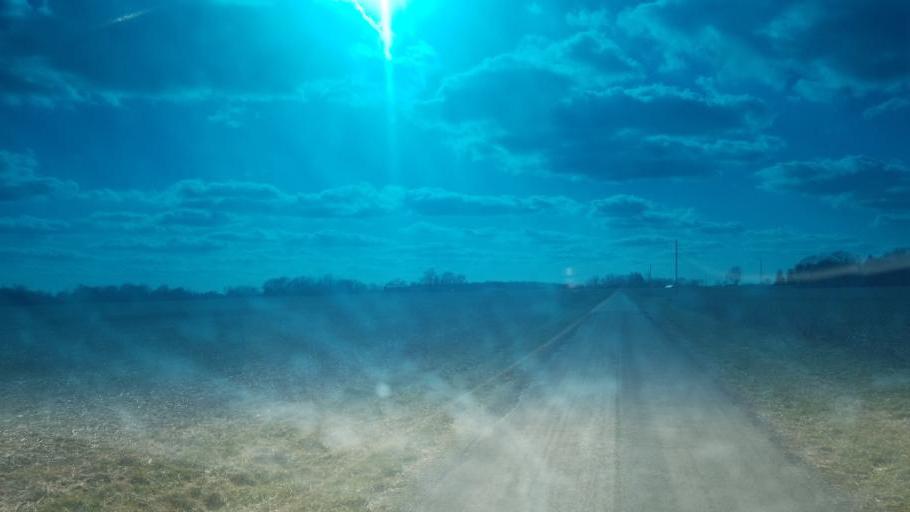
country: US
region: Ohio
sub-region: Highland County
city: Greenfield
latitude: 39.3168
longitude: -83.4201
